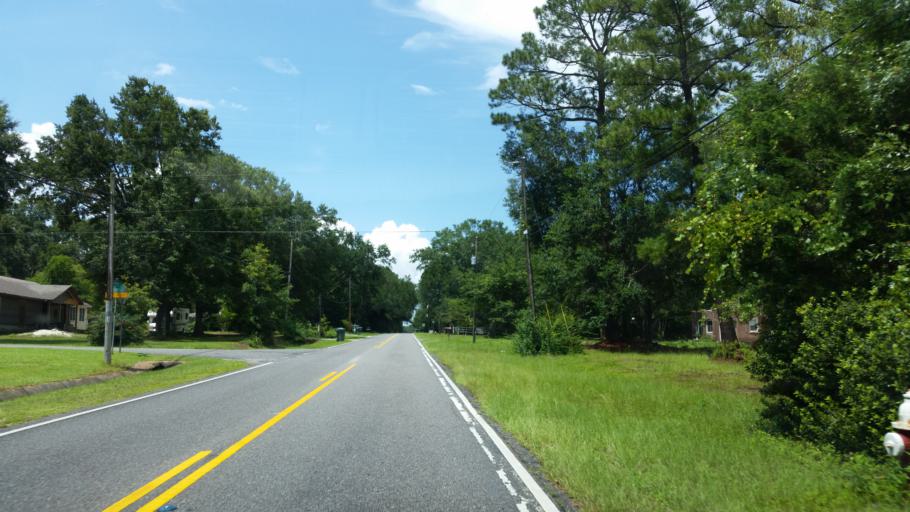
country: US
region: Florida
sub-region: Escambia County
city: Gonzalez
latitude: 30.5544
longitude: -87.2998
